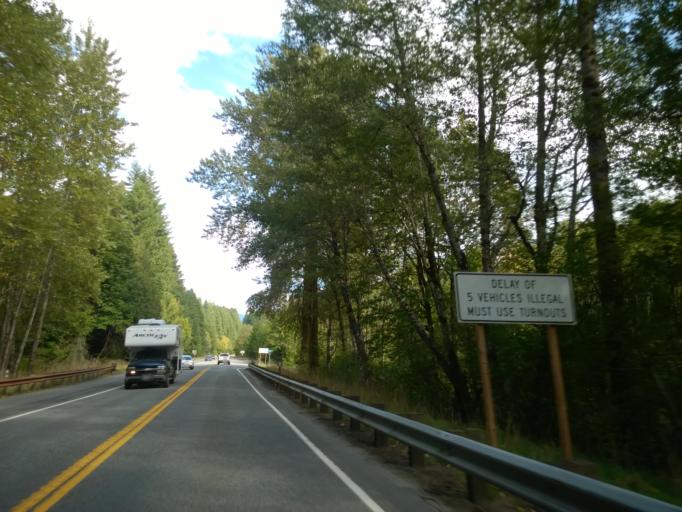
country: US
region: Washington
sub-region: Snohomish County
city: Gold Bar
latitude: 47.7121
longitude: -121.3218
